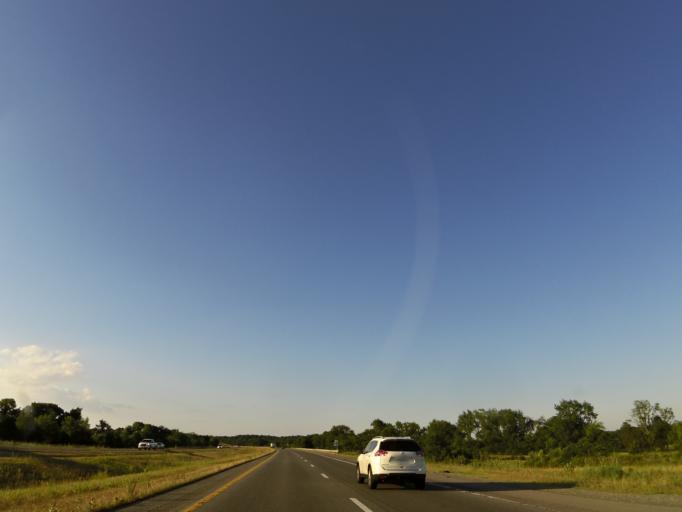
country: US
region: Tennessee
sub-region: Rutherford County
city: Smyrna
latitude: 35.9930
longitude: -86.4334
